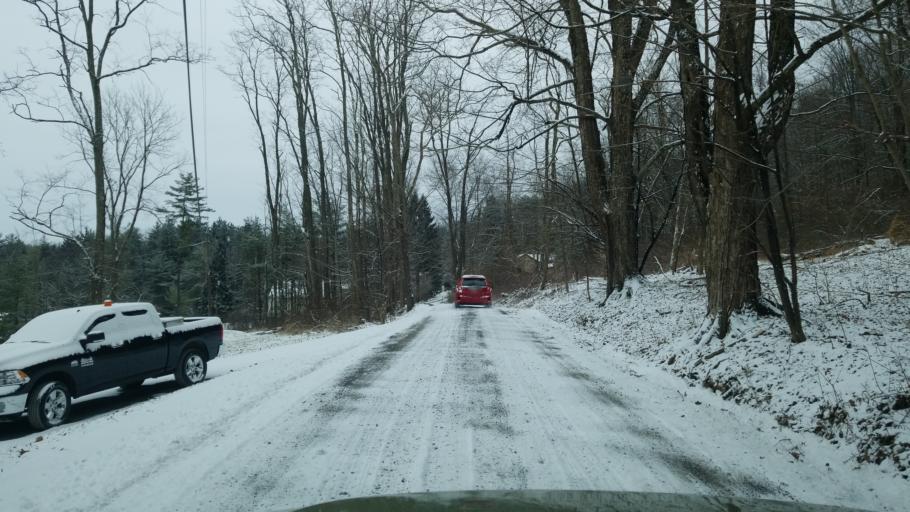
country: US
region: Pennsylvania
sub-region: Centre County
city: Centre Hall
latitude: 40.7690
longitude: -77.6801
